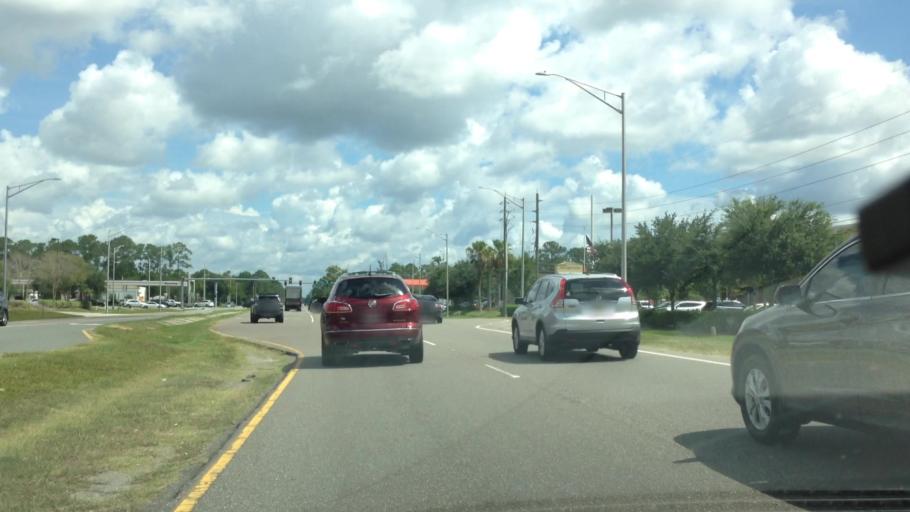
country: US
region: Florida
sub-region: Duval County
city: Jacksonville Beach
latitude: 30.2858
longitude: -81.4589
